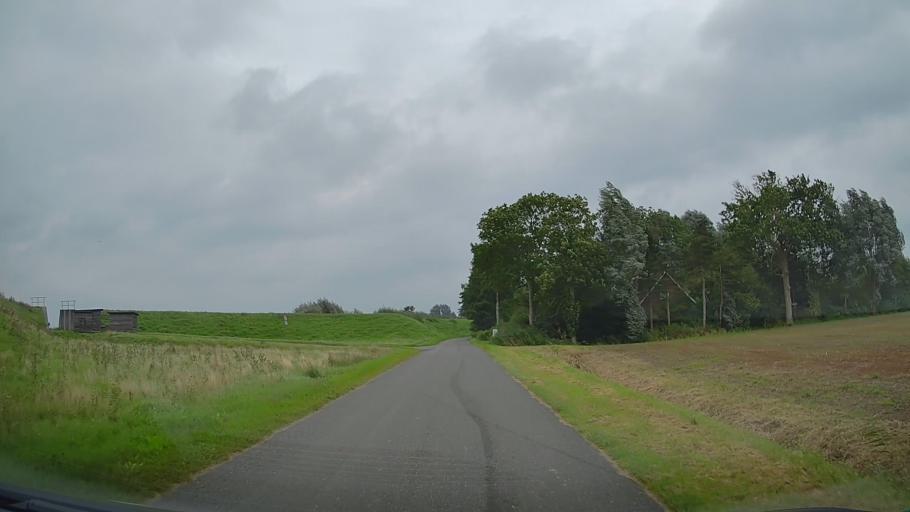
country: DE
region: Lower Saxony
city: Balje
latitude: 53.8303
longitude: 9.1516
